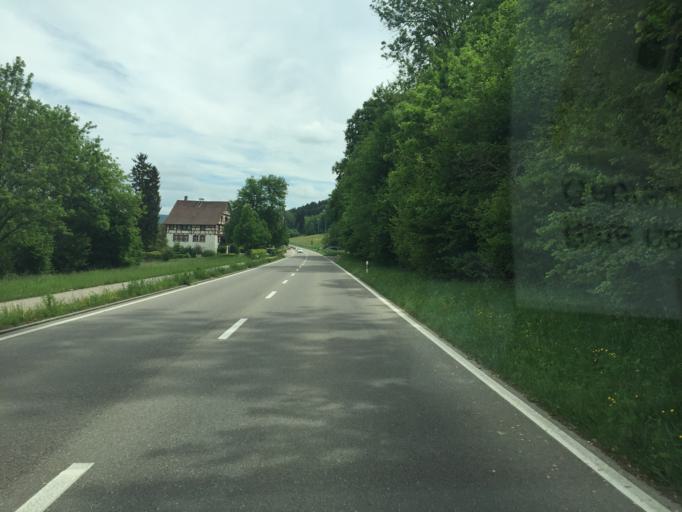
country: DE
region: Baden-Wuerttemberg
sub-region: Freiburg Region
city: Gailingen
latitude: 47.6755
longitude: 8.7834
